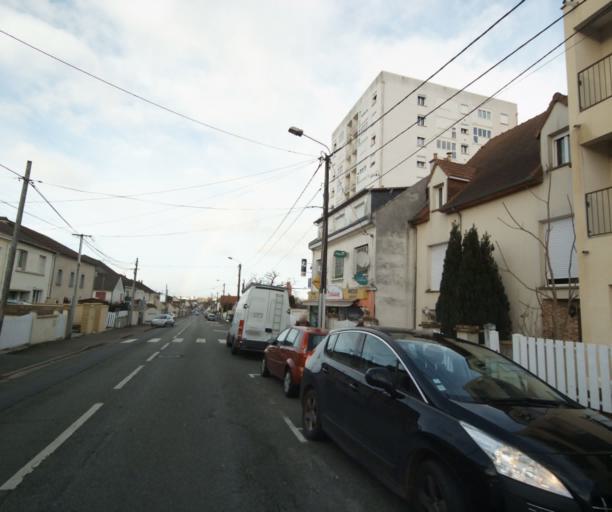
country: FR
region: Pays de la Loire
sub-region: Departement de la Sarthe
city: Le Mans
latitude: 47.9737
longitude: 0.2110
